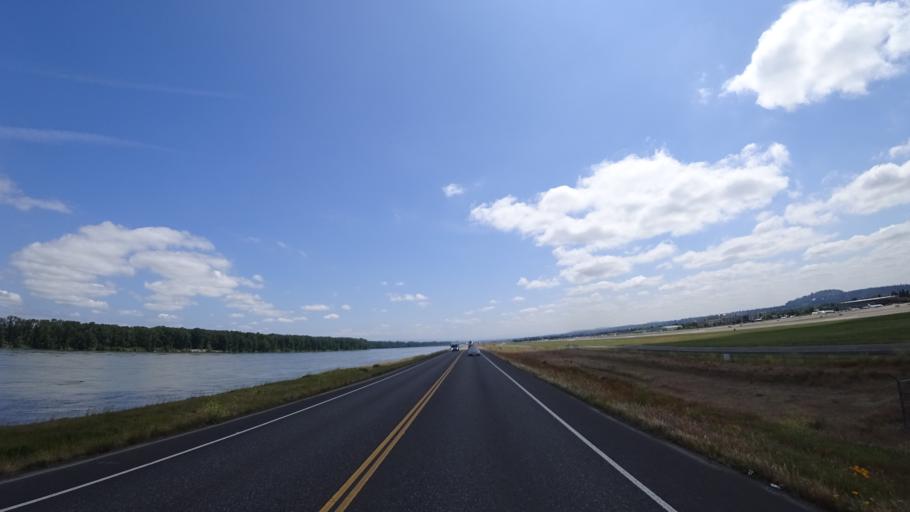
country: US
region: Washington
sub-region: Clark County
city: Orchards
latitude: 45.5909
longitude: -122.5793
